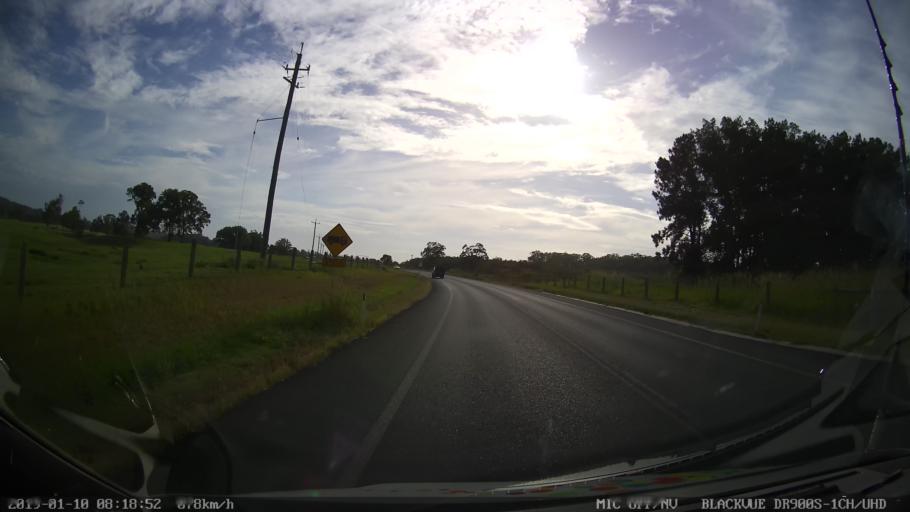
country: AU
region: New South Wales
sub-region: Bellingen
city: Bellingen
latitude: -30.4676
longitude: 152.9630
